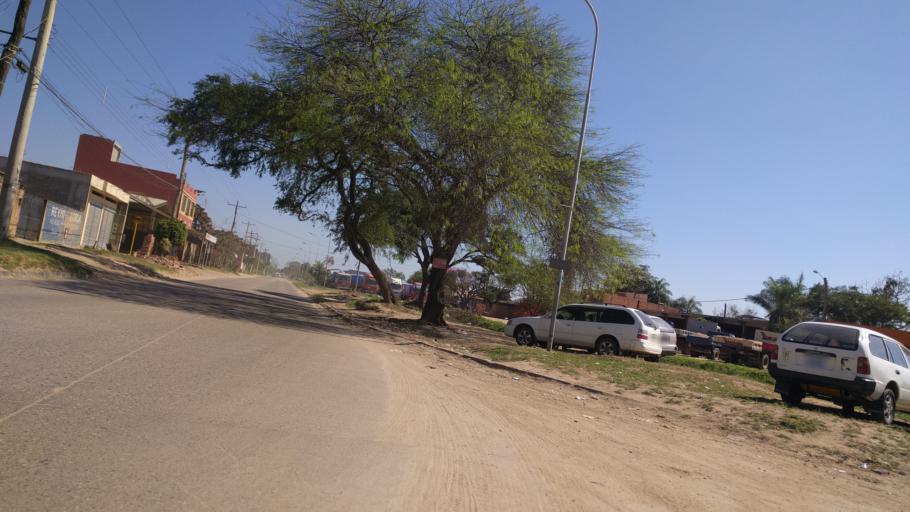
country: BO
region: Santa Cruz
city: Santa Cruz de la Sierra
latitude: -17.8522
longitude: -63.1989
